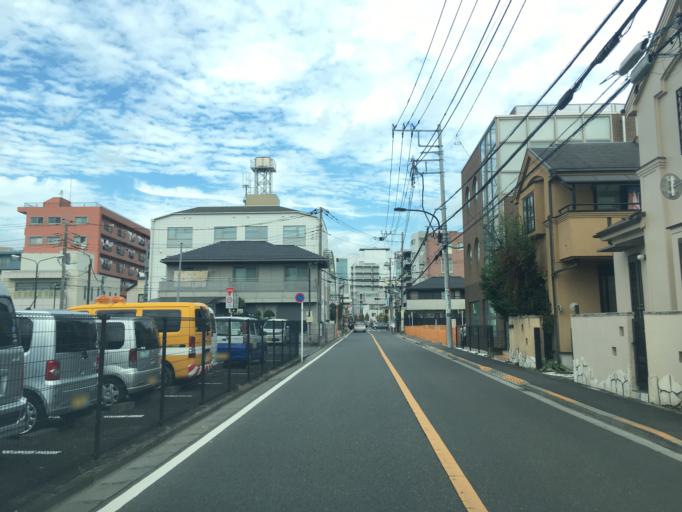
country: JP
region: Tokyo
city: Chofugaoka
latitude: 35.6481
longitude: 139.5411
